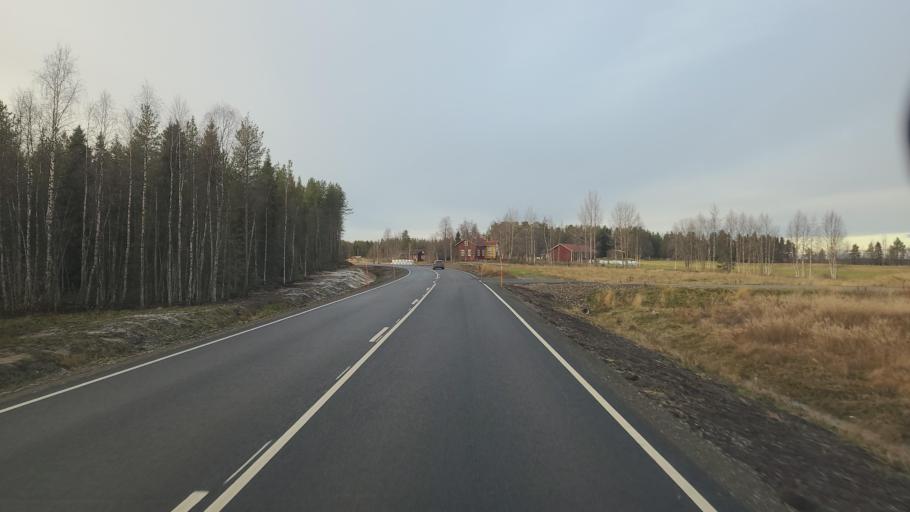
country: FI
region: Lapland
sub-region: Tunturi-Lappi
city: Kittilae
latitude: 67.8769
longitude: 24.8860
